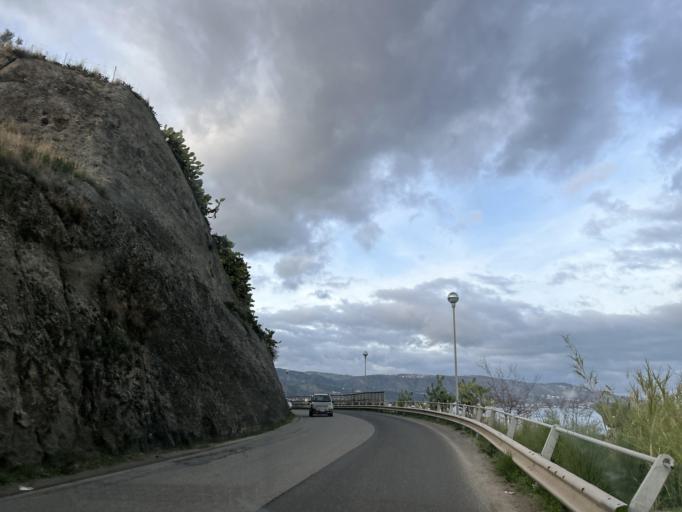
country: IT
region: Calabria
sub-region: Provincia di Catanzaro
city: Soverato Superiore
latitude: 38.6984
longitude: 16.5401
